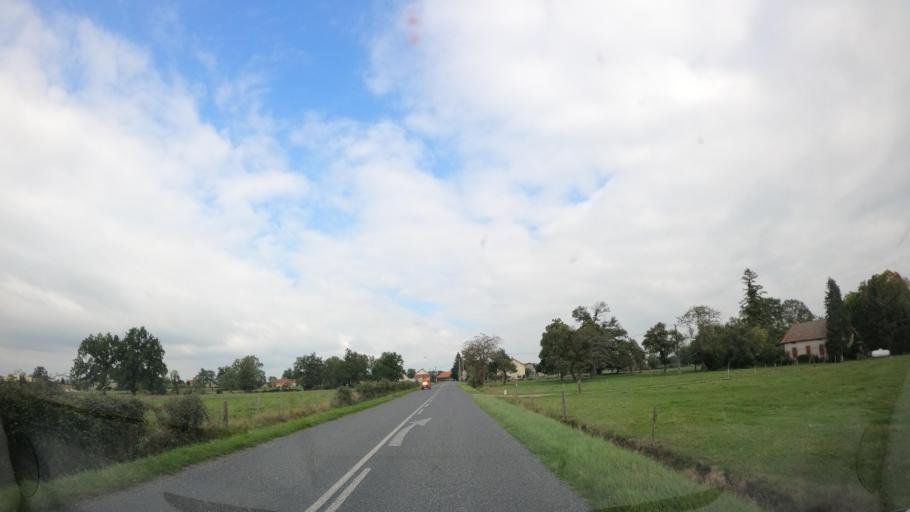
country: FR
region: Auvergne
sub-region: Departement de l'Allier
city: Saint-Gerand-le-Puy
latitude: 46.2192
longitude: 3.5135
